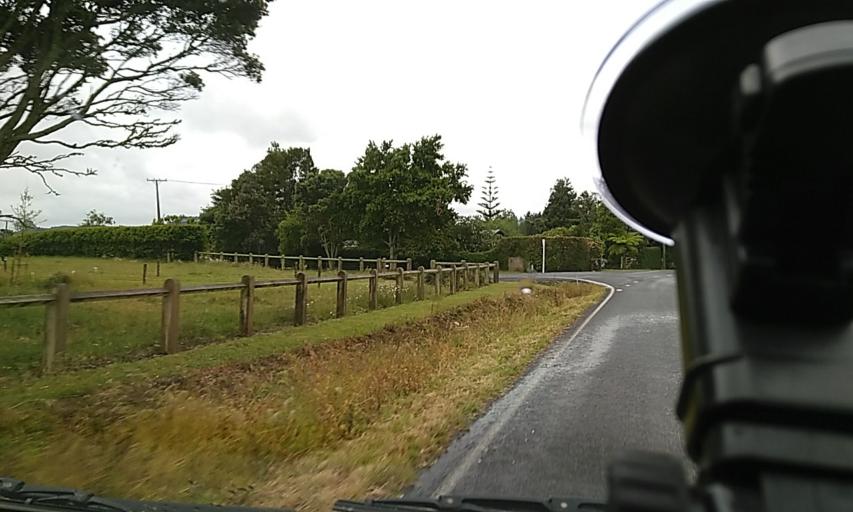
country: NZ
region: Auckland
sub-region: Auckland
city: Pukekohe East
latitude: -37.3282
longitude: 174.9150
